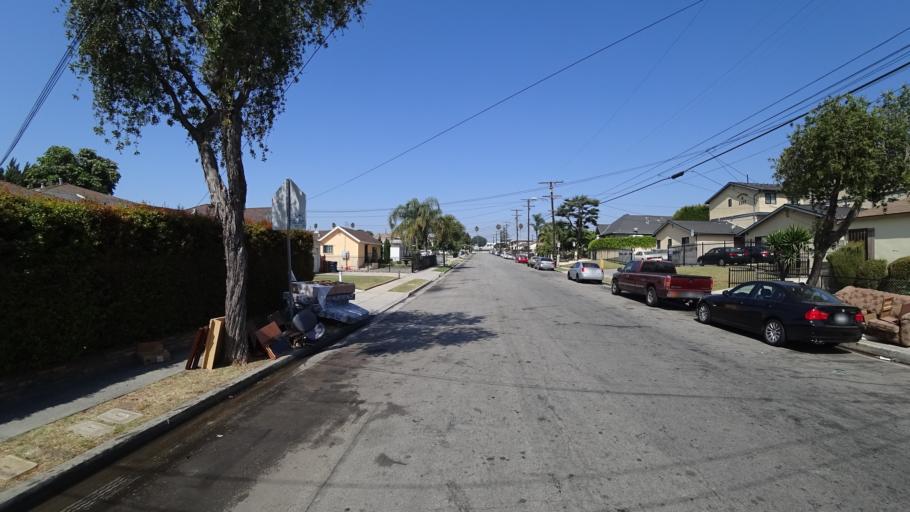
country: US
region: California
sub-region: Los Angeles County
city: Westmont
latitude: 33.9373
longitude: -118.2974
